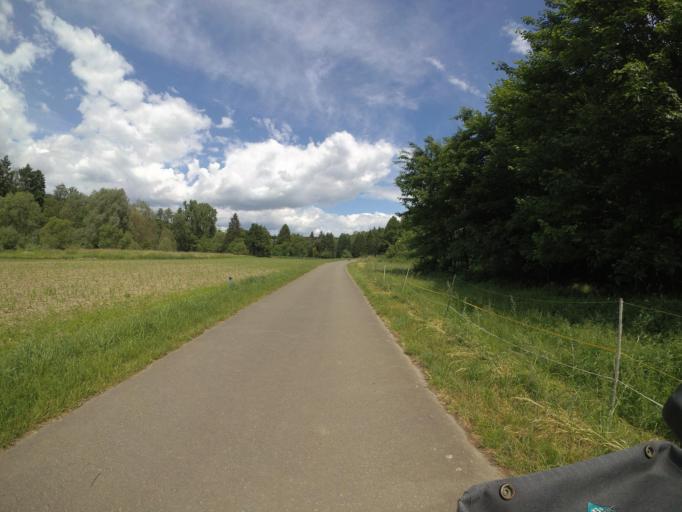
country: DE
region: Rheinland-Pfalz
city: Lauterecken
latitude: 49.6461
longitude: 7.5859
